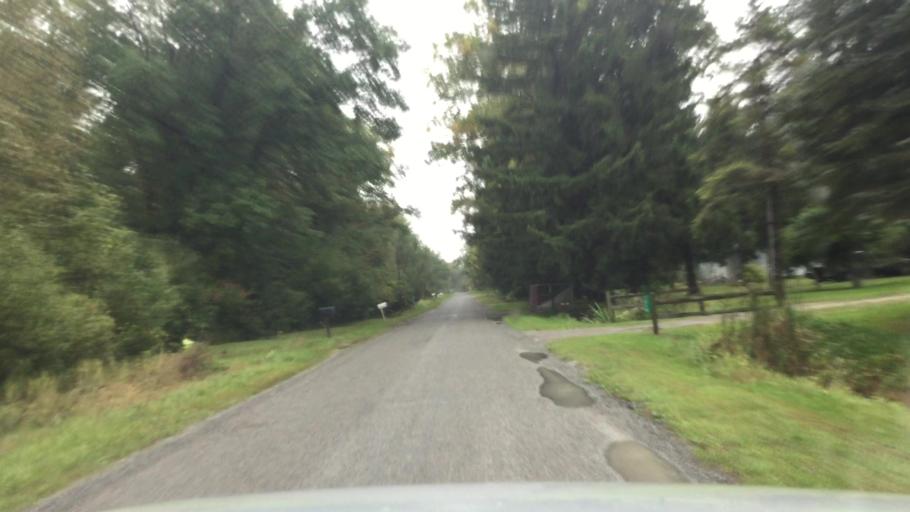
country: US
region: Michigan
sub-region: Saginaw County
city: Bridgeport
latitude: 43.3146
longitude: -83.8354
